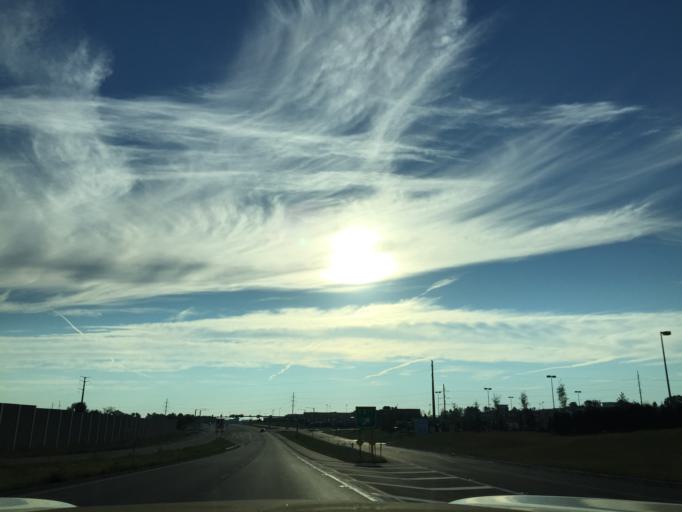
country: US
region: Pennsylvania
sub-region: Lehigh County
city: Wescosville
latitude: 40.5648
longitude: -75.5679
